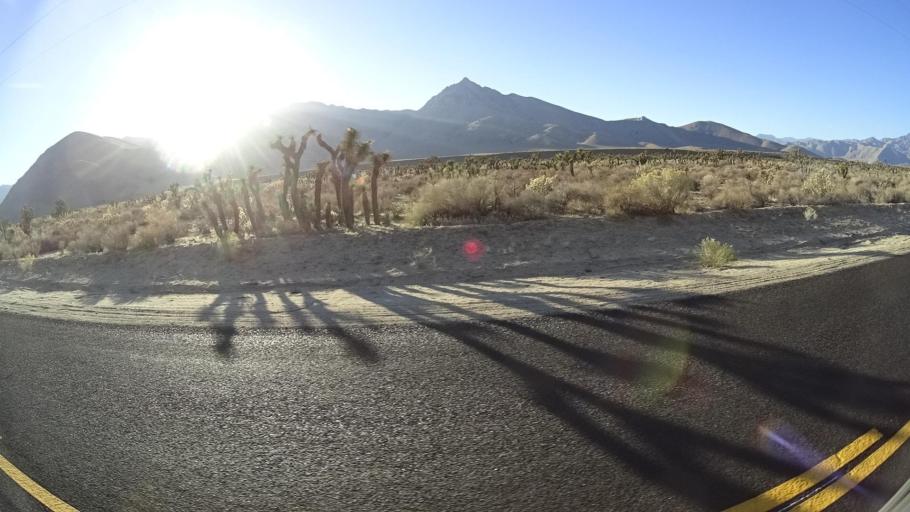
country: US
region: California
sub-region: Kern County
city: Weldon
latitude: 35.6234
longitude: -118.2435
